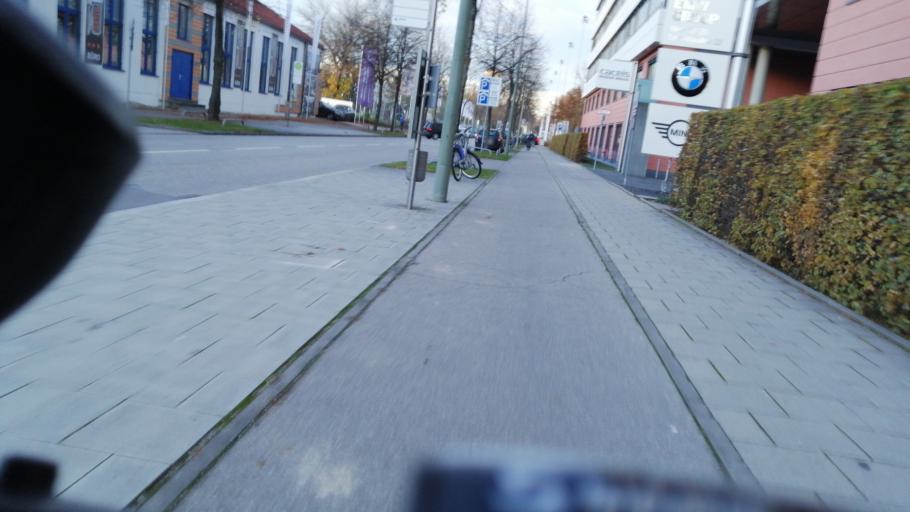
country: DE
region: Bavaria
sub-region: Upper Bavaria
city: Unterfoehring
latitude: 48.1953
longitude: 11.6091
